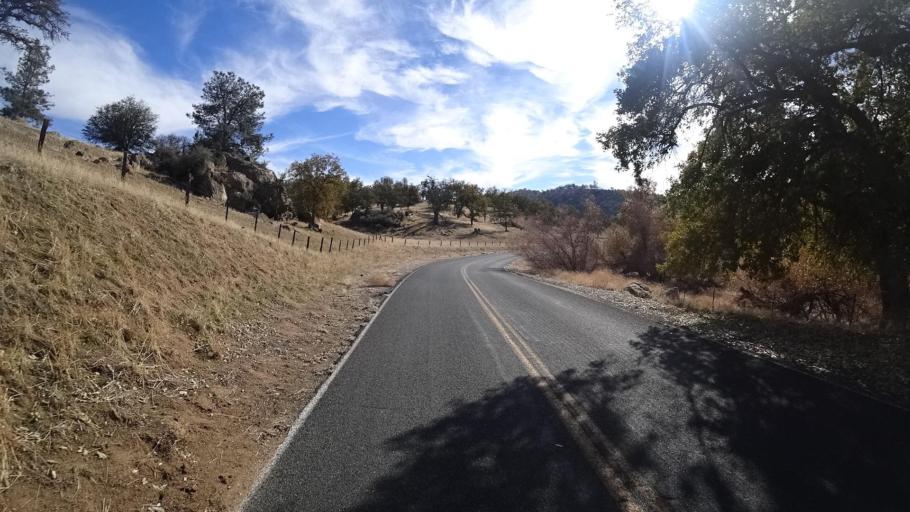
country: US
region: California
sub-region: Kern County
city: Alta Sierra
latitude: 35.7104
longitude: -118.7270
